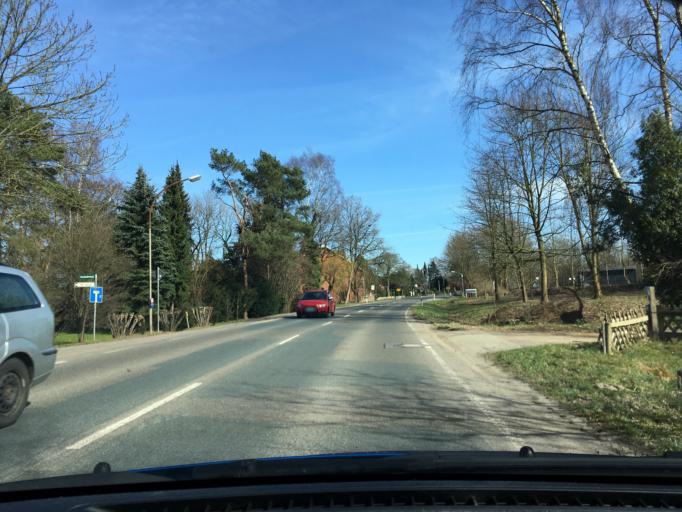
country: DE
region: Schleswig-Holstein
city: Escheburg
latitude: 53.4284
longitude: 10.3140
